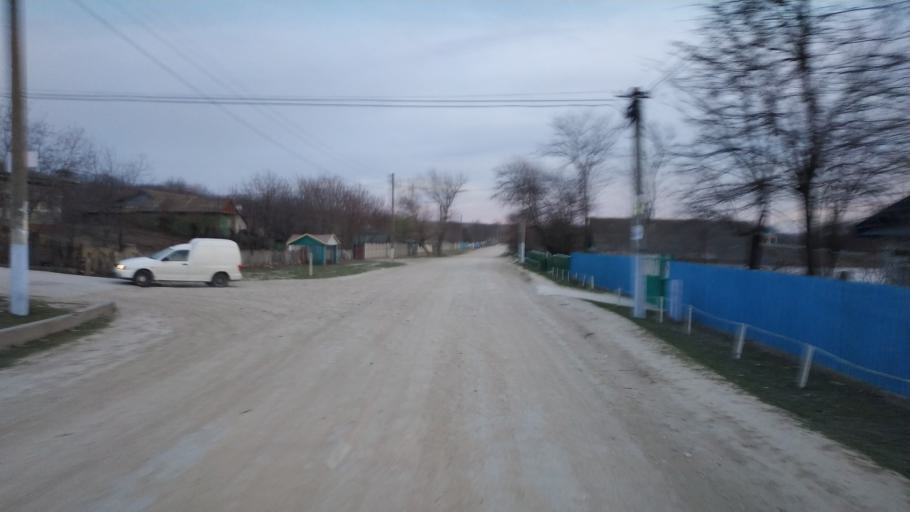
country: MD
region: Hincesti
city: Dancu
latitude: 46.7388
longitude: 28.2139
